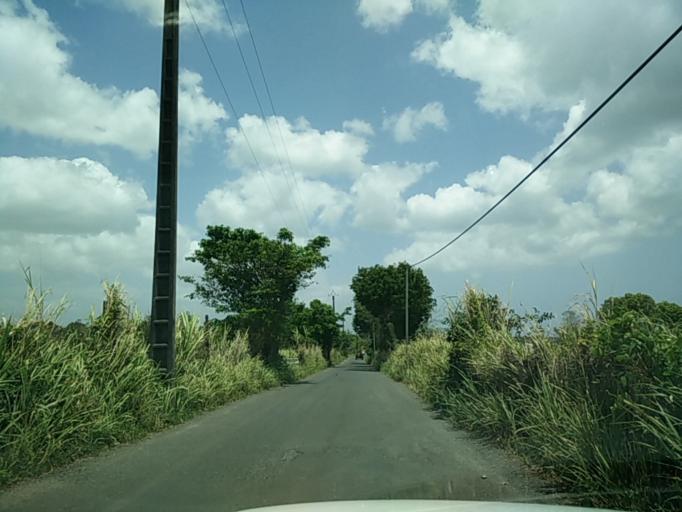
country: GP
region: Guadeloupe
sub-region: Guadeloupe
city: Les Abymes
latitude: 16.2803
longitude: -61.5129
